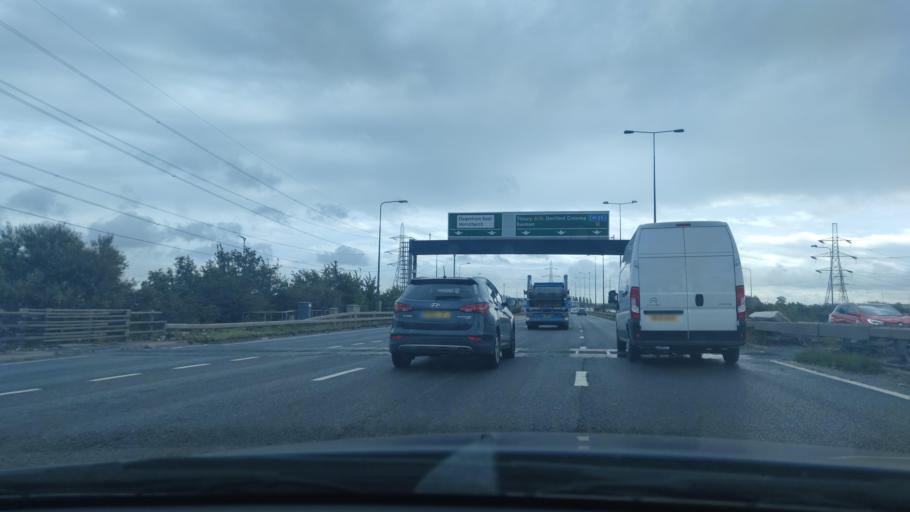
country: GB
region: England
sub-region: Greater London
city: Dagenham
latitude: 51.5213
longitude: 0.1634
